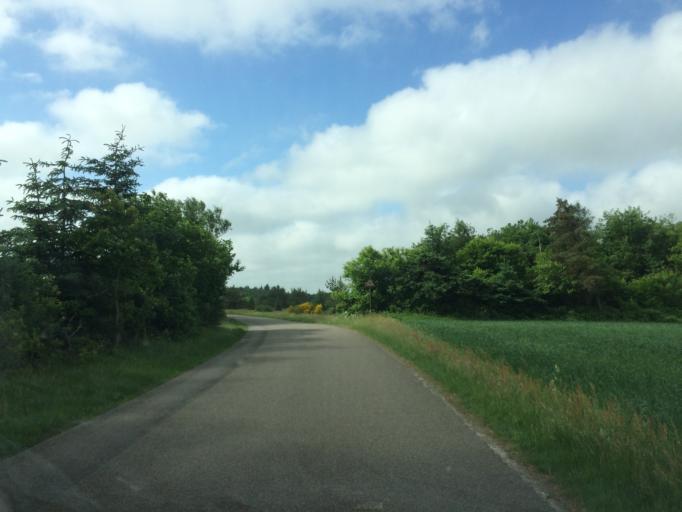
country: DK
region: Central Jutland
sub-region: Holstebro Kommune
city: Ulfborg
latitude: 56.2276
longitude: 8.4352
